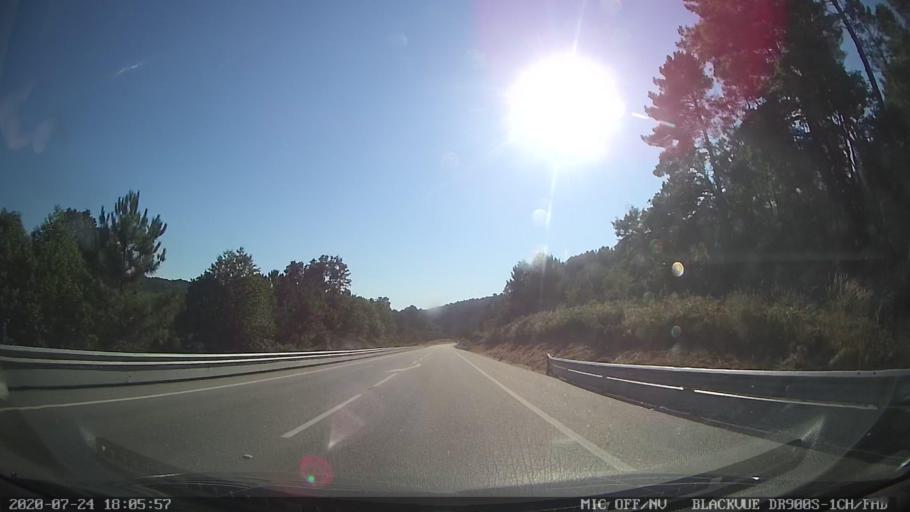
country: PT
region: Vila Real
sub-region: Sabrosa
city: Vilela
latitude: 41.2661
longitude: -7.6670
